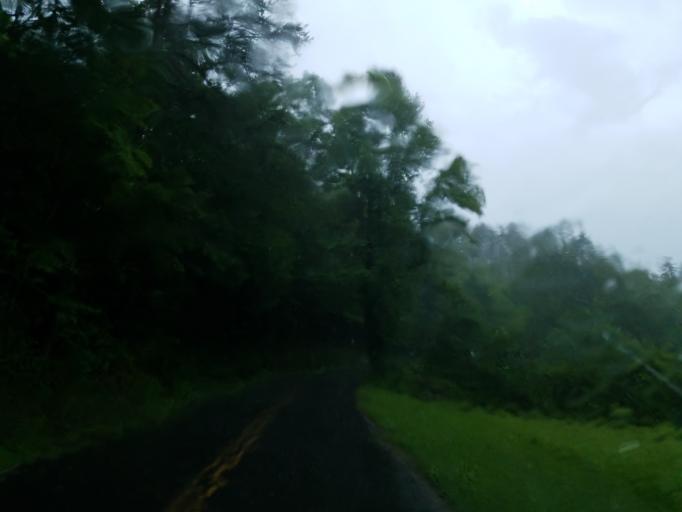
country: US
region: Georgia
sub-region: Fannin County
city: Blue Ridge
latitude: 34.7859
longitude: -84.2958
